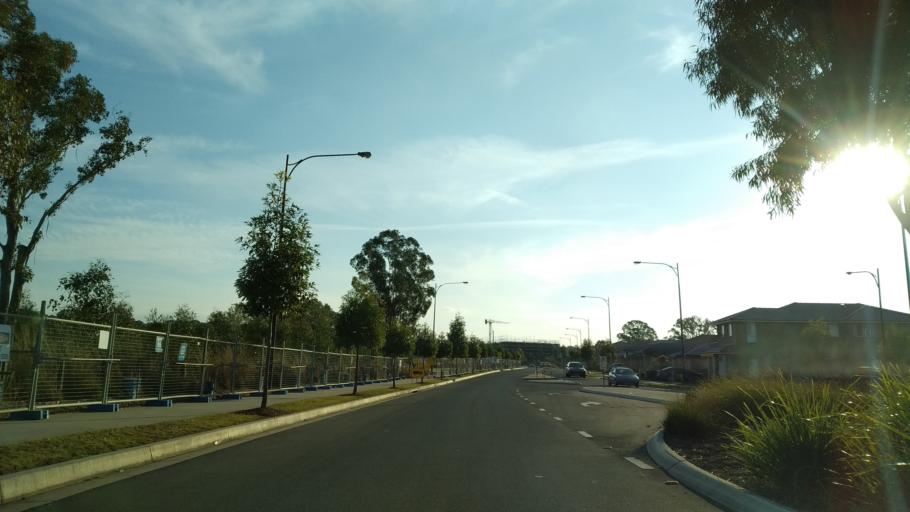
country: AU
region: New South Wales
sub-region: Penrith Municipality
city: Werrington Downs
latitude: -33.7287
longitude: 150.7335
